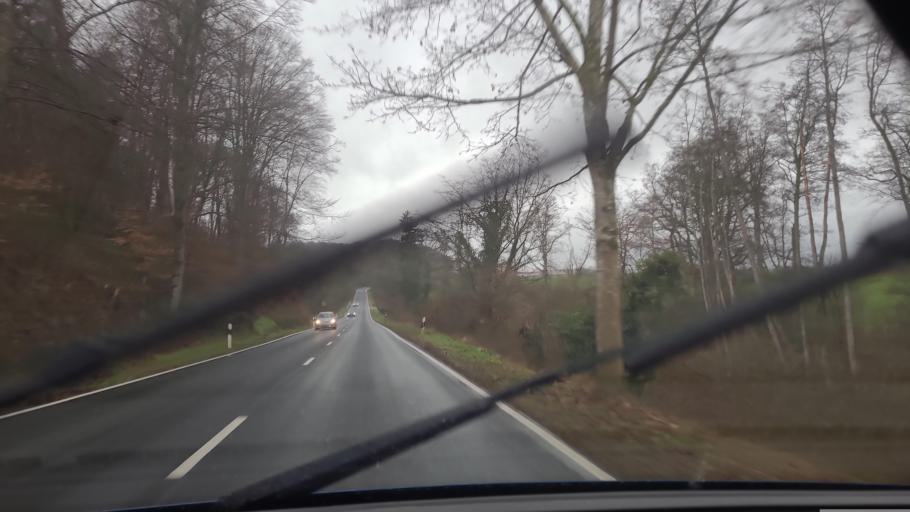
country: LU
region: Luxembourg
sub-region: Canton de Capellen
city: Kehlen
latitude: 49.6505
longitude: 6.0281
